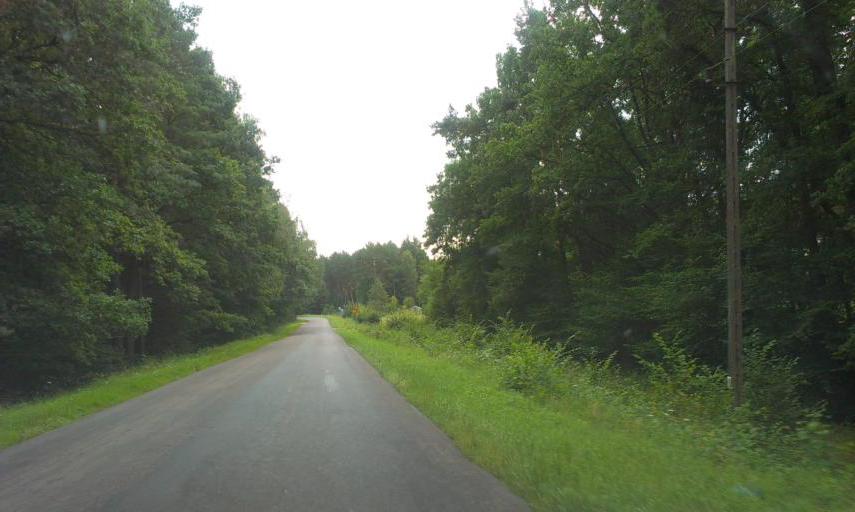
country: PL
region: West Pomeranian Voivodeship
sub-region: Powiat swidwinski
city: Polczyn-Zdroj
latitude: 53.7844
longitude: 16.1408
